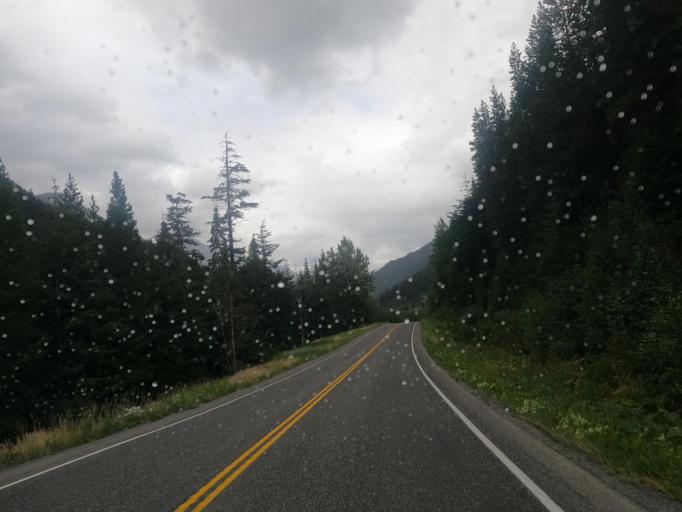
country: CA
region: British Columbia
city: Lillooet
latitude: 50.4950
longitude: -122.1910
